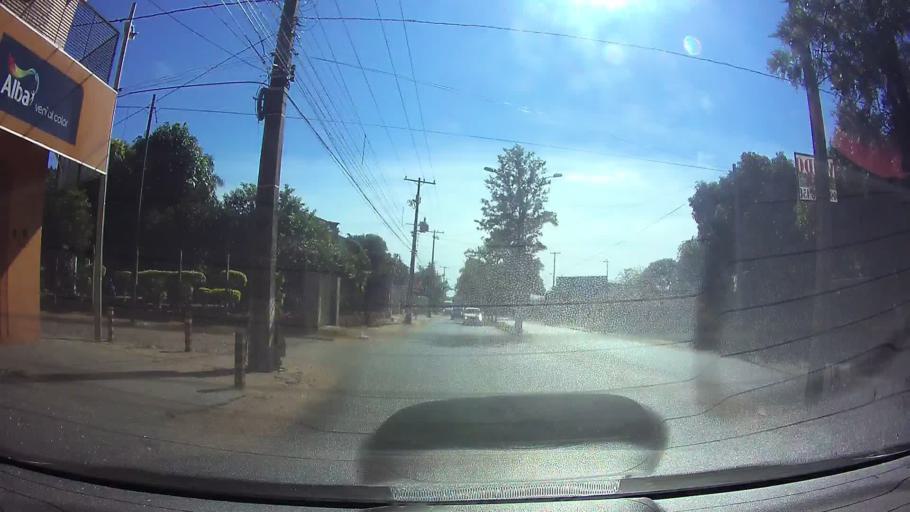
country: PY
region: Central
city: Villa Elisa
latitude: -25.3714
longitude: -57.5789
